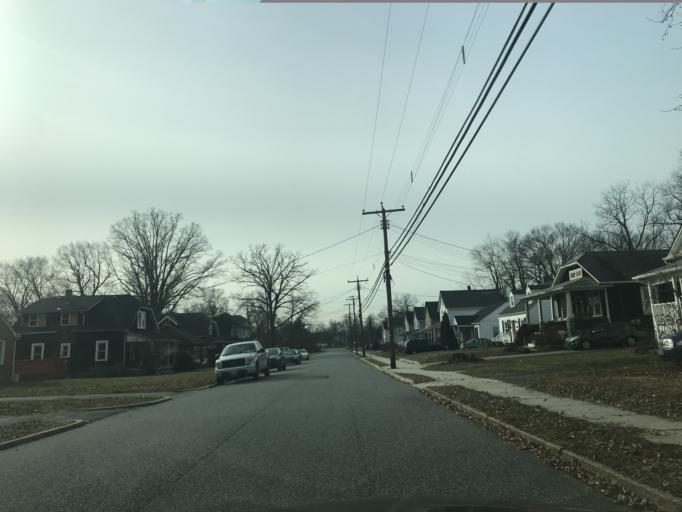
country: US
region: Maryland
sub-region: Harford County
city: Aberdeen
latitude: 39.5135
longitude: -76.1682
